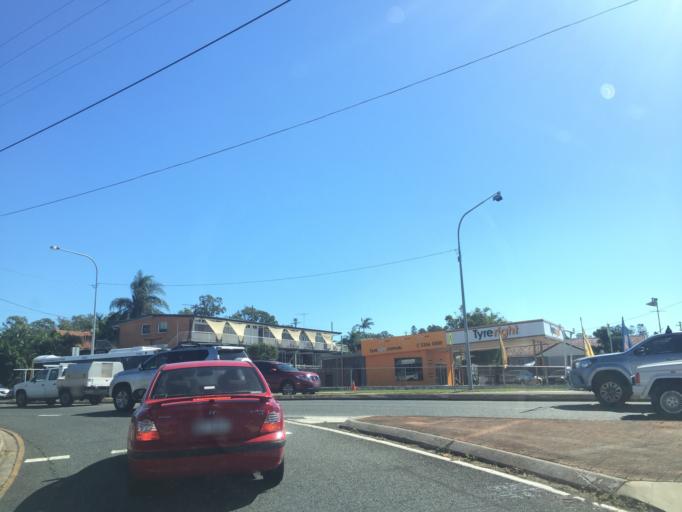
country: AU
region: Queensland
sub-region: Brisbane
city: Stafford
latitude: -27.4106
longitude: 153.0167
